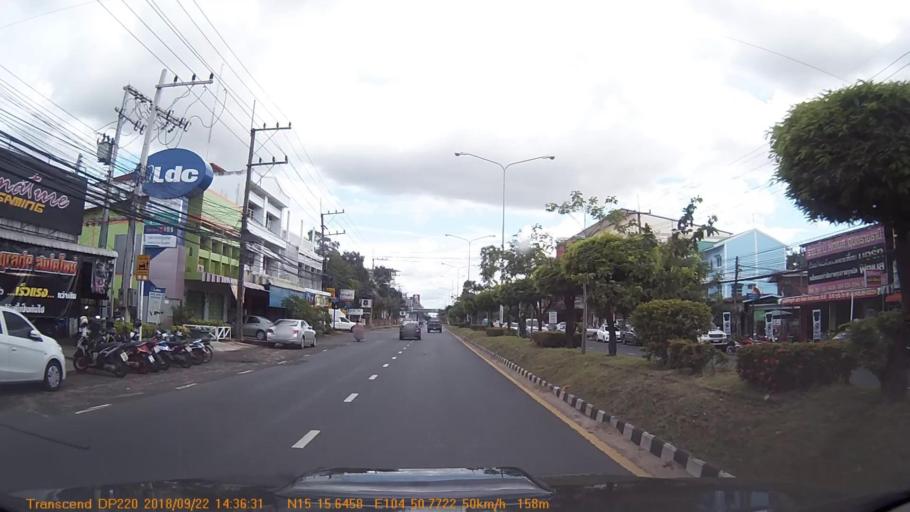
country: TH
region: Changwat Ubon Ratchathani
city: Ubon Ratchathani
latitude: 15.2604
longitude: 104.8463
